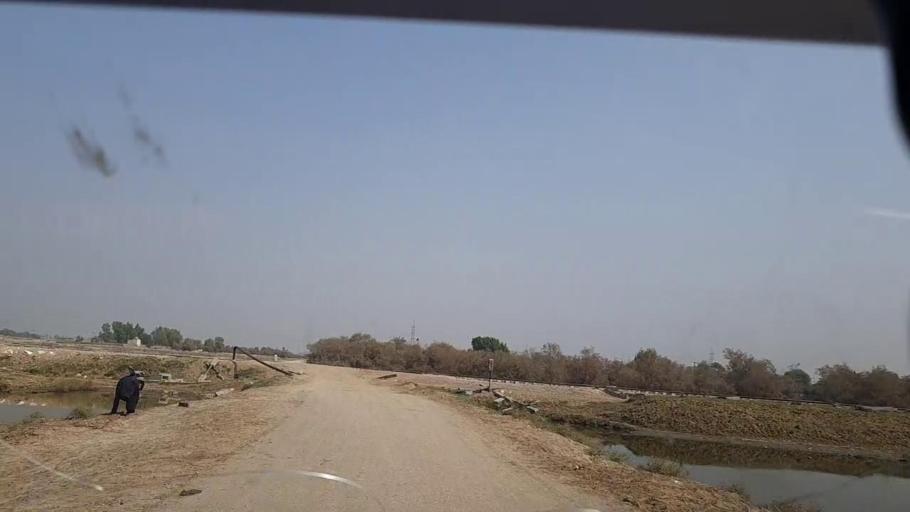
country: PK
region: Sindh
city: Shikarpur
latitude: 28.0273
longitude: 68.6197
